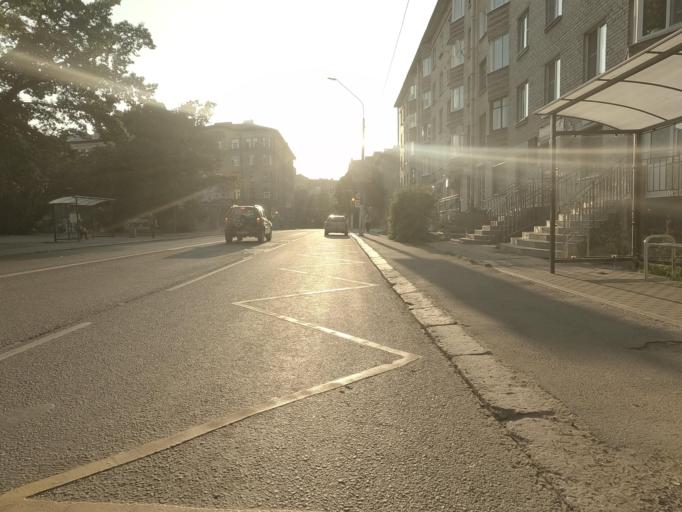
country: RU
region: Leningrad
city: Vyborg
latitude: 60.7106
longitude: 28.7604
